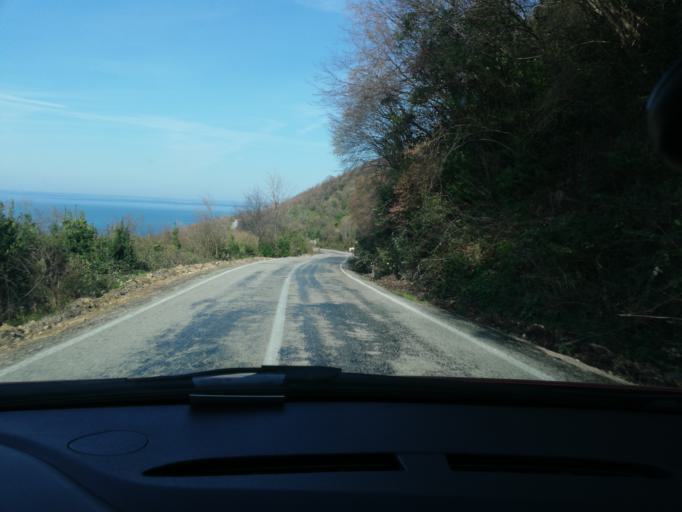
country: TR
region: Bartin
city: Kurucasile
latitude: 41.8536
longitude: 32.7753
